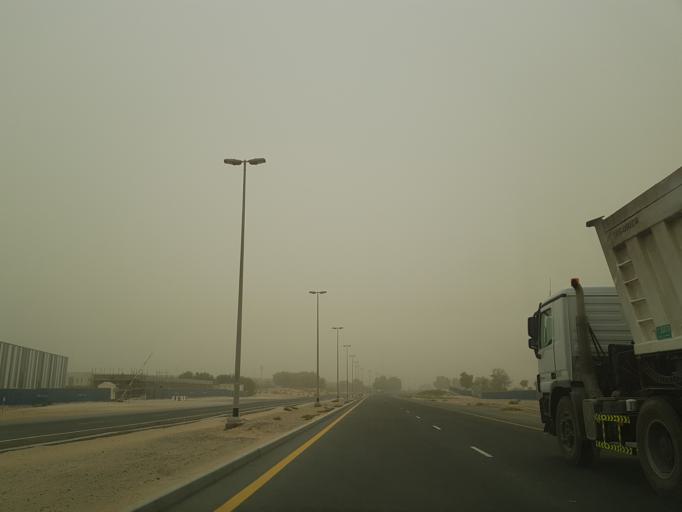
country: AE
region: Dubai
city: Dubai
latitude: 25.1479
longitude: 55.2859
